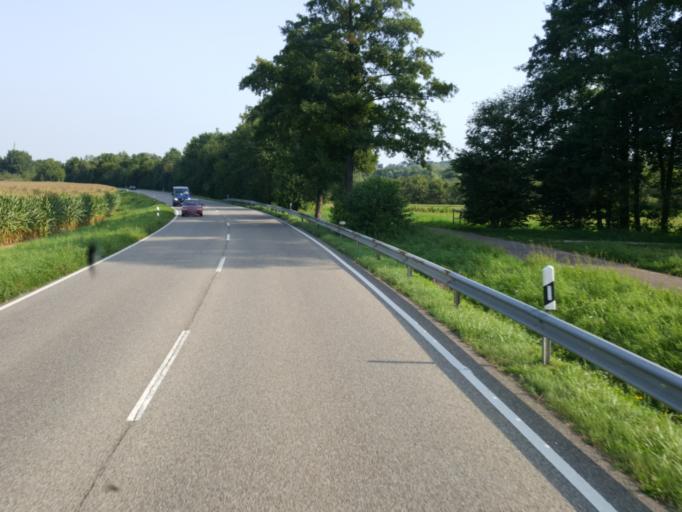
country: DE
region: Baden-Wuerttemberg
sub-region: Karlsruhe Region
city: Sinzheim
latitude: 48.7490
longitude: 8.1670
